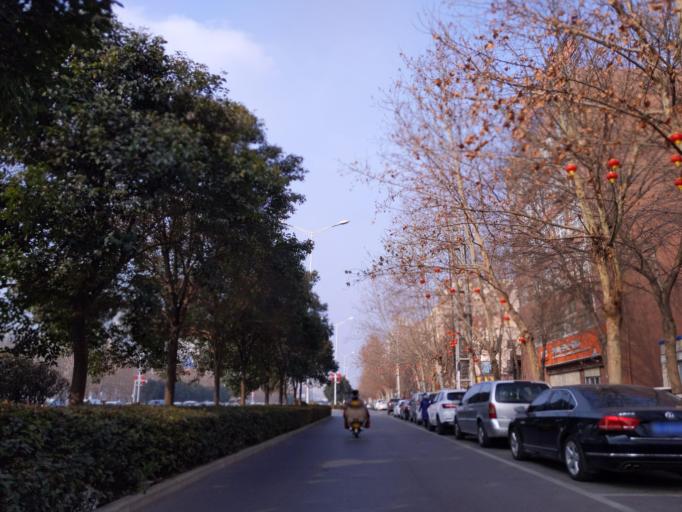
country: CN
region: Henan Sheng
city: Puyang
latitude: 35.7823
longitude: 115.0209
